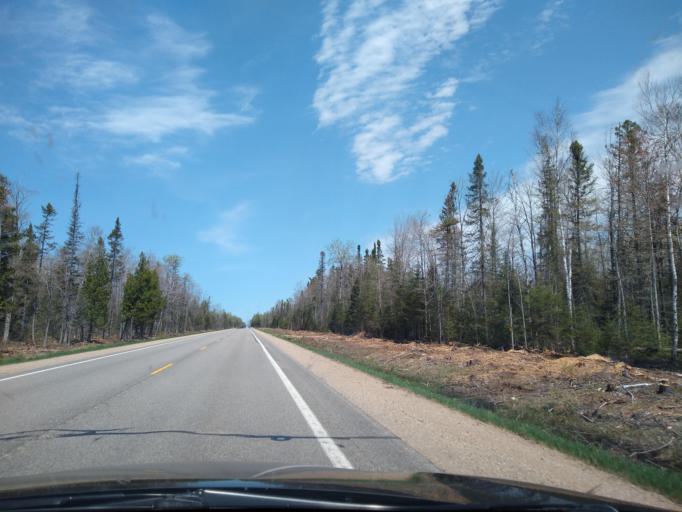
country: US
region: Michigan
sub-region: Delta County
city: Gladstone
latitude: 46.0406
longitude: -86.9816
